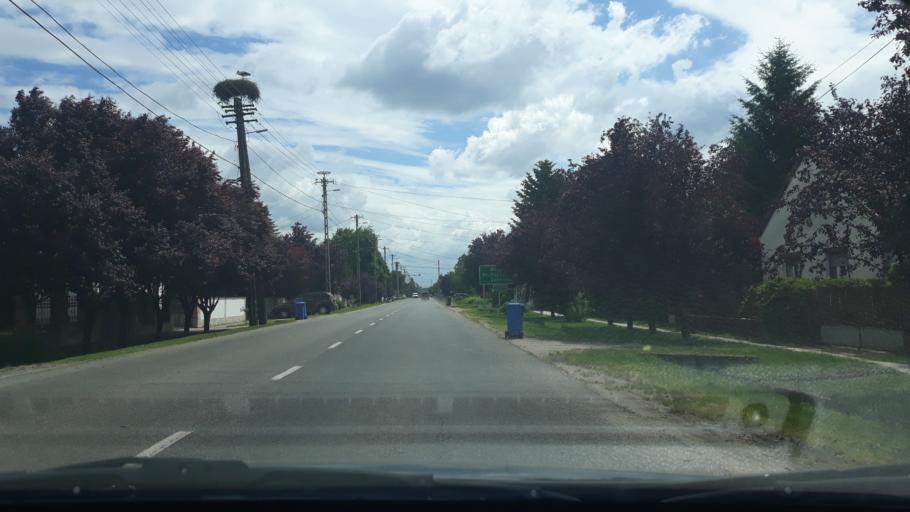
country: HU
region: Hajdu-Bihar
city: Biharkeresztes
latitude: 47.1318
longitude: 21.7189
